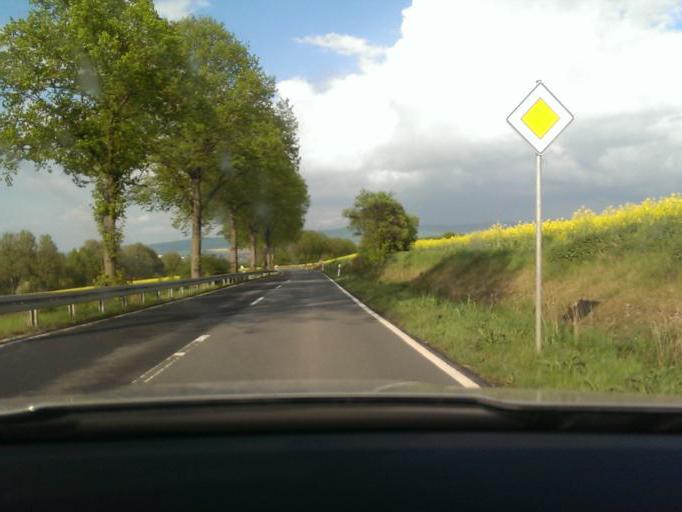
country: DE
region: Lower Saxony
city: Pohle
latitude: 52.2425
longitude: 9.3004
